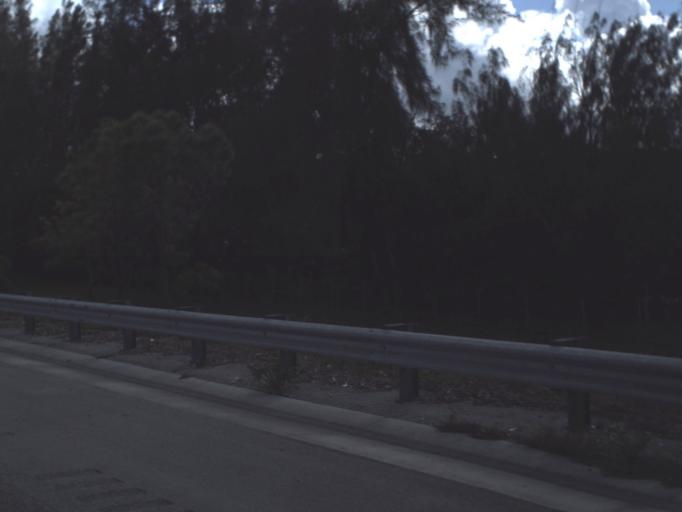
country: US
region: Florida
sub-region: Broward County
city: Coconut Creek
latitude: 26.2583
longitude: -80.1670
